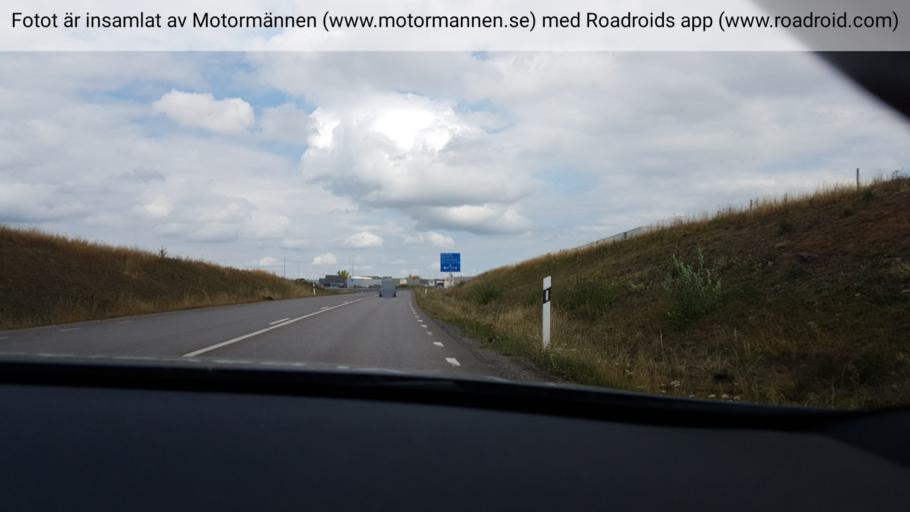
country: SE
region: Vaestra Goetaland
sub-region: Falkopings Kommun
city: Falkoeping
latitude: 58.1467
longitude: 13.5623
